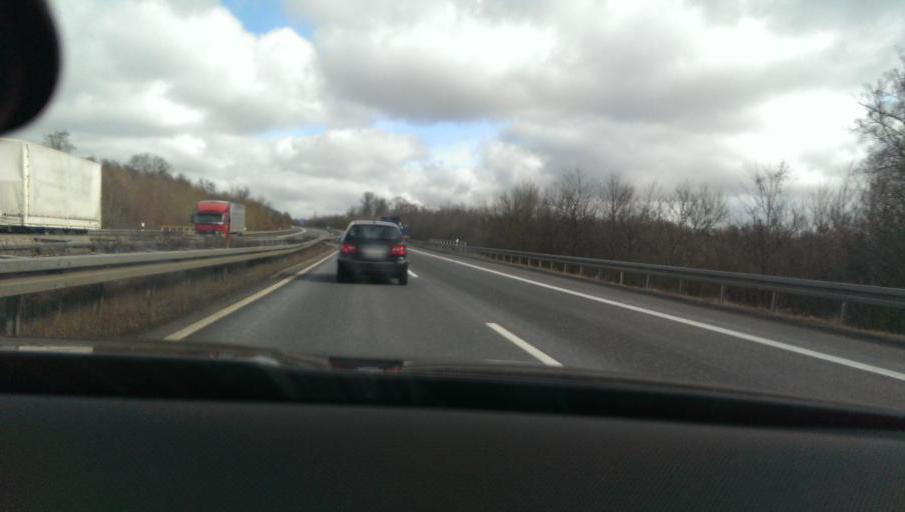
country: DE
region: Hesse
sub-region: Regierungsbezirk Darmstadt
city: Schluchtern
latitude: 50.3704
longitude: 9.5093
